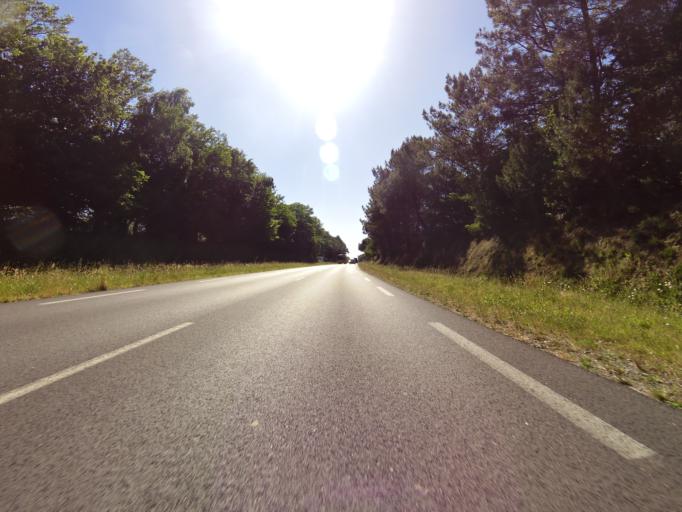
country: FR
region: Pays de la Loire
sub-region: Departement de la Loire-Atlantique
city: Asserac
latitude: 47.4786
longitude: -2.4149
